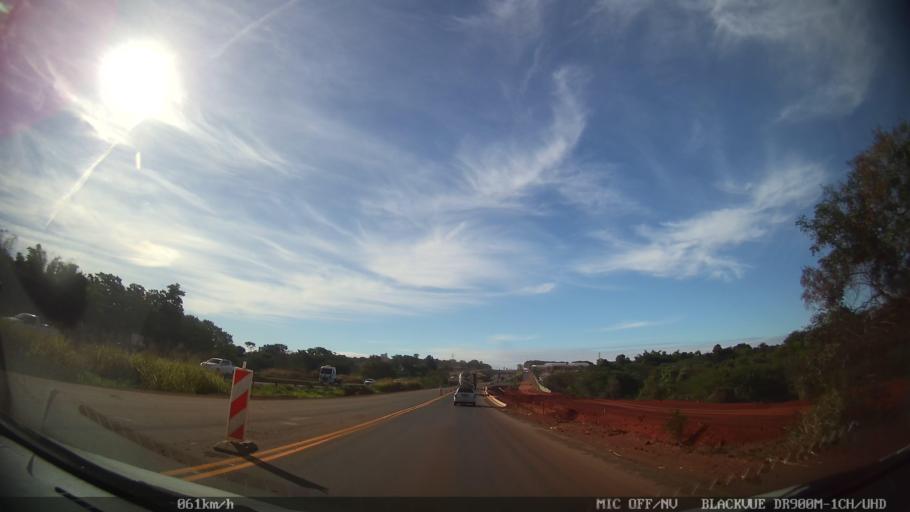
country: BR
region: Sao Paulo
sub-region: Sao Jose Do Rio Preto
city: Sao Jose do Rio Preto
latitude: -20.7766
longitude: -49.3524
